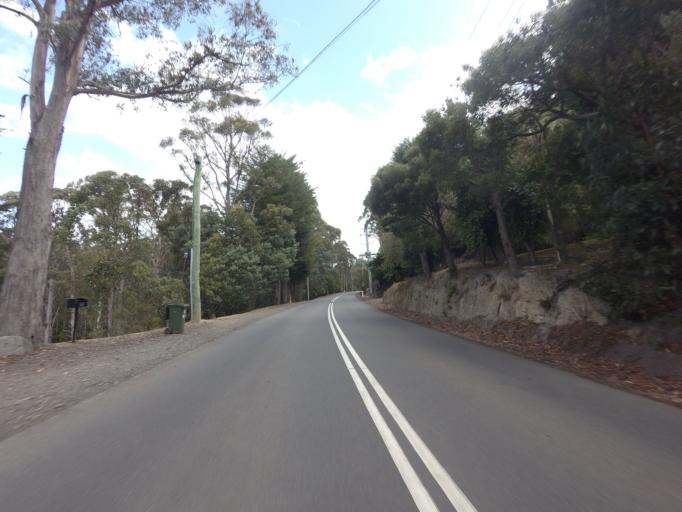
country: AU
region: Tasmania
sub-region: Hobart
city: Dynnyrne
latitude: -42.9173
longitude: 147.2693
